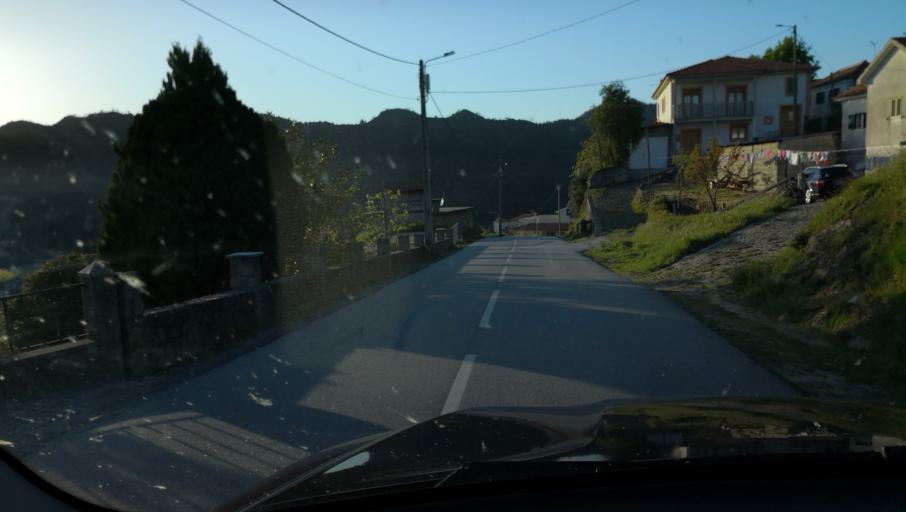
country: PT
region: Vila Real
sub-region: Mondim de Basto
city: Mondim de Basto
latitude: 41.4125
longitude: -7.8783
